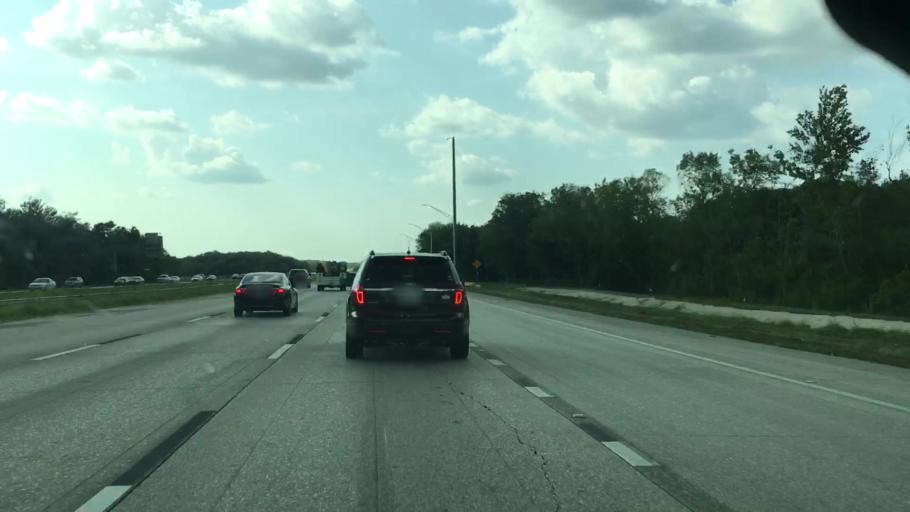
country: US
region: Florida
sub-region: Hillsborough County
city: Mango
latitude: 28.0206
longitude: -82.3330
